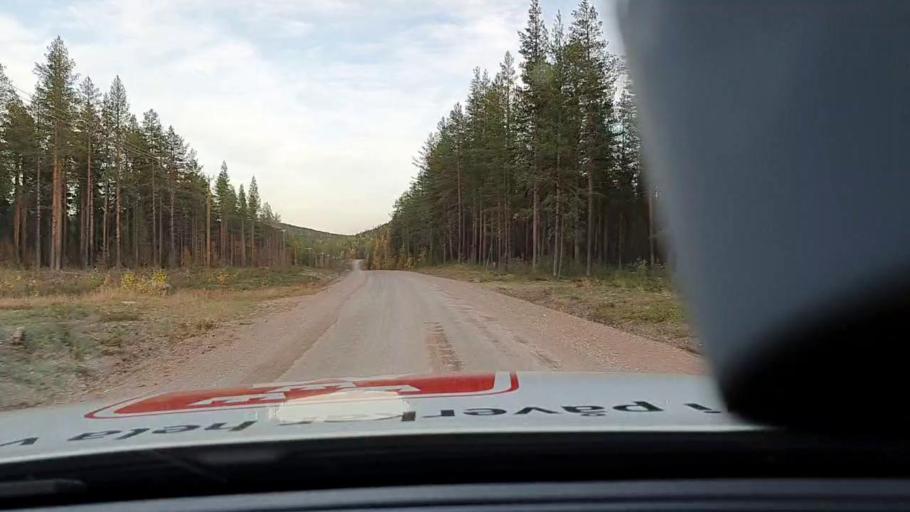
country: SE
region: Norrbotten
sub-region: Overkalix Kommun
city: OEverkalix
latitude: 66.3278
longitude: 22.5950
